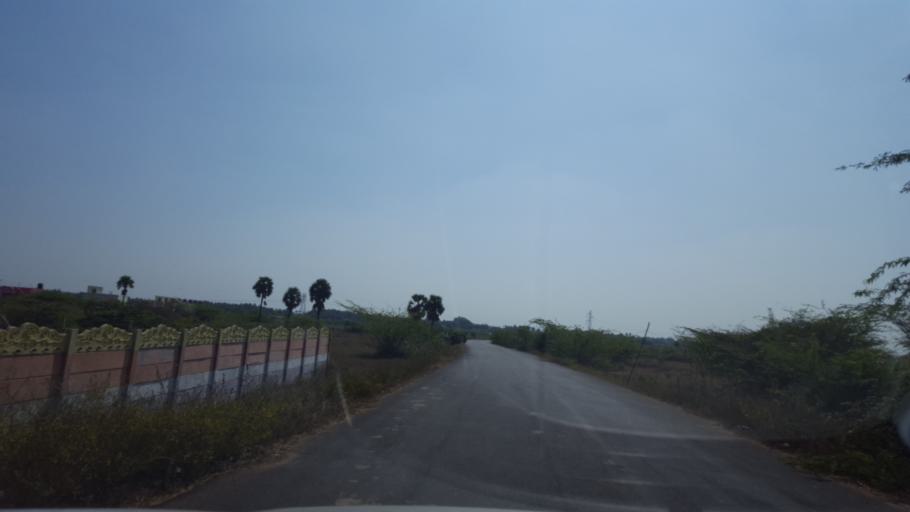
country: IN
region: Tamil Nadu
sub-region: Kancheepuram
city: Kanchipuram
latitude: 12.8555
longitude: 79.7533
